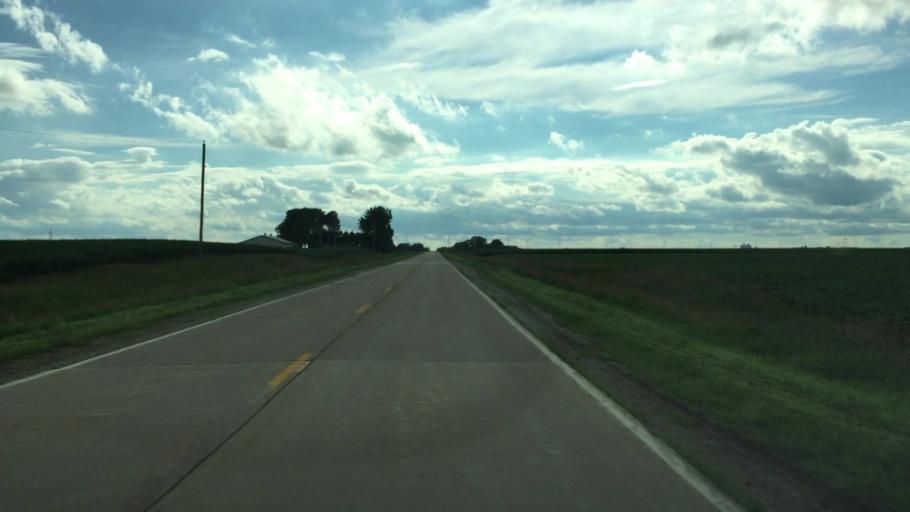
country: US
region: Iowa
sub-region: Jasper County
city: Prairie City
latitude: 41.5806
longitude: -93.1702
